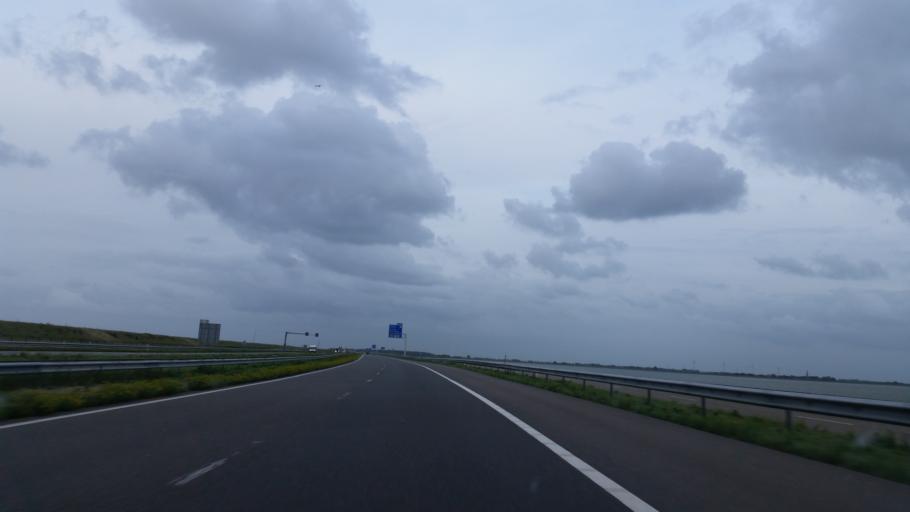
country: NL
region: Friesland
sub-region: Sudwest Fryslan
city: Makkum
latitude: 53.0775
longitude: 5.3504
